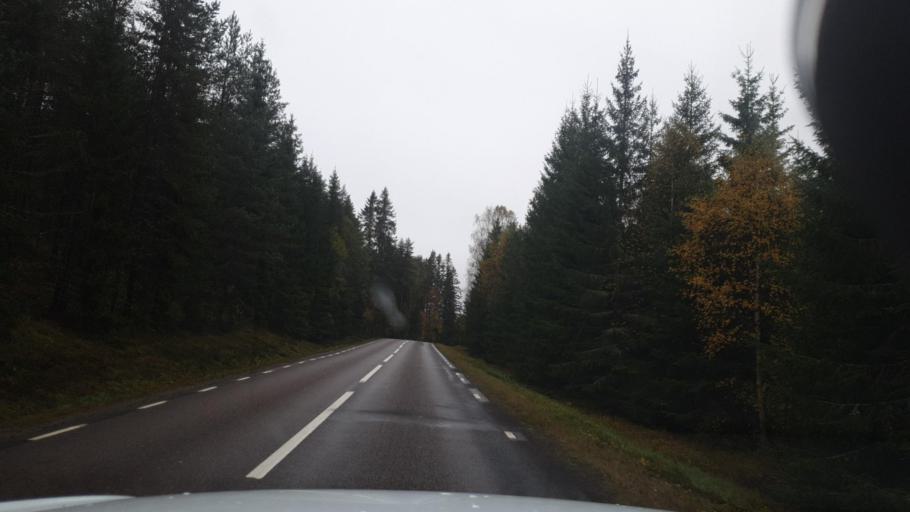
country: SE
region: Vaermland
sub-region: Eda Kommun
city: Amotfors
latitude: 59.6670
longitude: 12.3826
